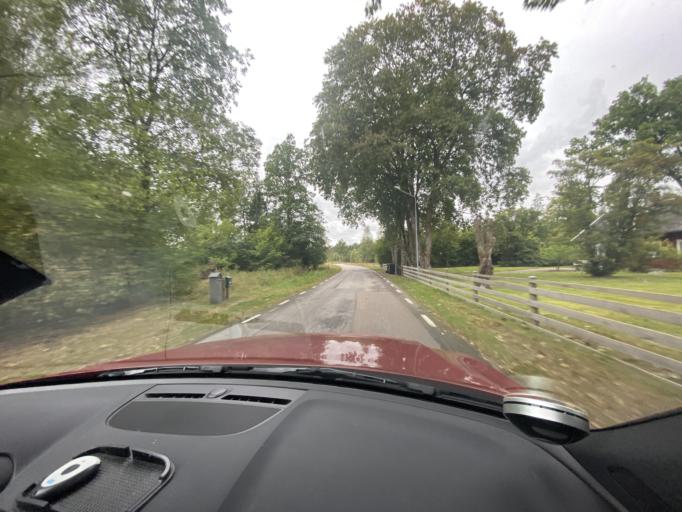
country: SE
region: Kronoberg
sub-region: Markaryds Kommun
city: Markaryd
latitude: 56.4946
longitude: 13.5755
